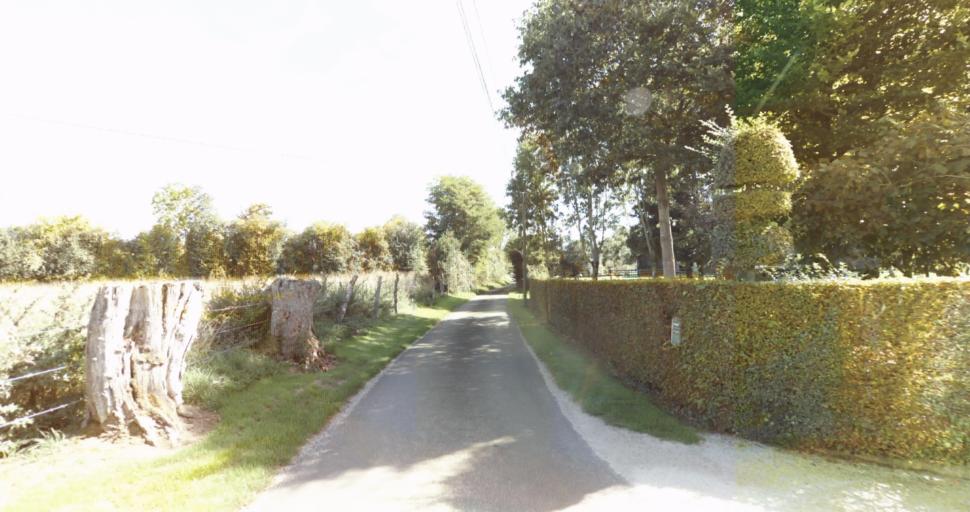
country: FR
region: Lower Normandy
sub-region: Departement de l'Orne
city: Gace
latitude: 48.7399
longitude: 0.2386
